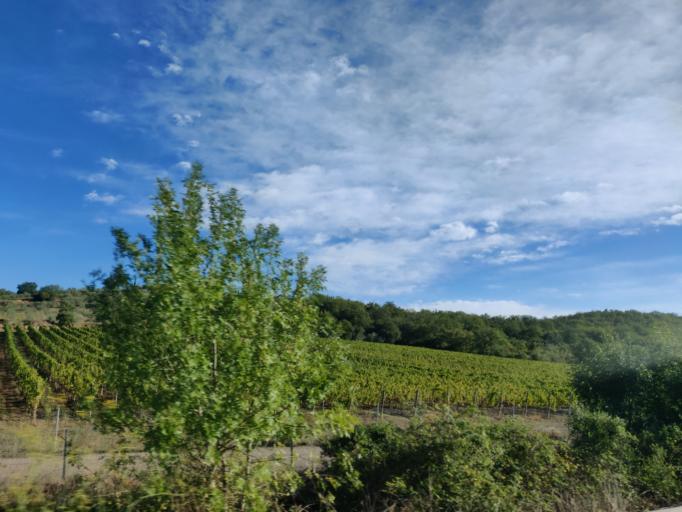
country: IT
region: Tuscany
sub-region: Provincia di Grosseto
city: Gavorrano
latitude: 42.9198
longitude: 10.9659
